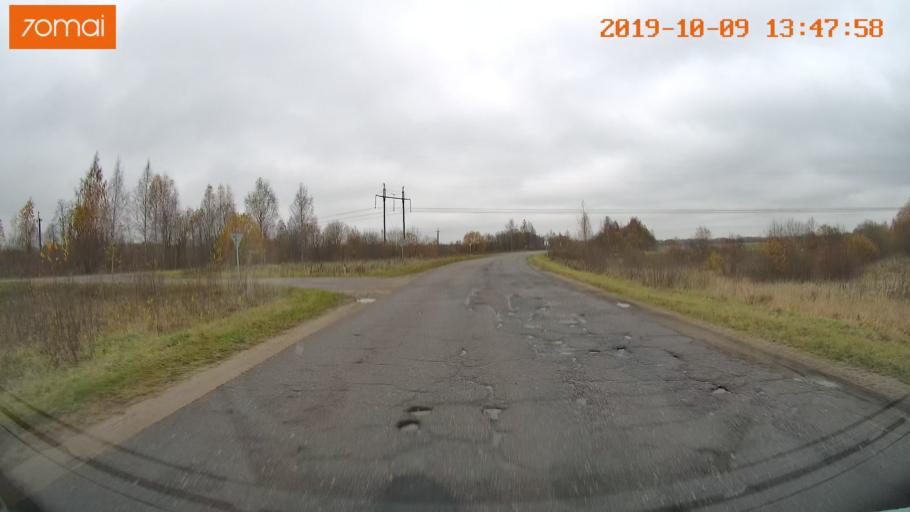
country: RU
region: Kostroma
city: Buy
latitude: 58.3970
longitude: 41.2277
